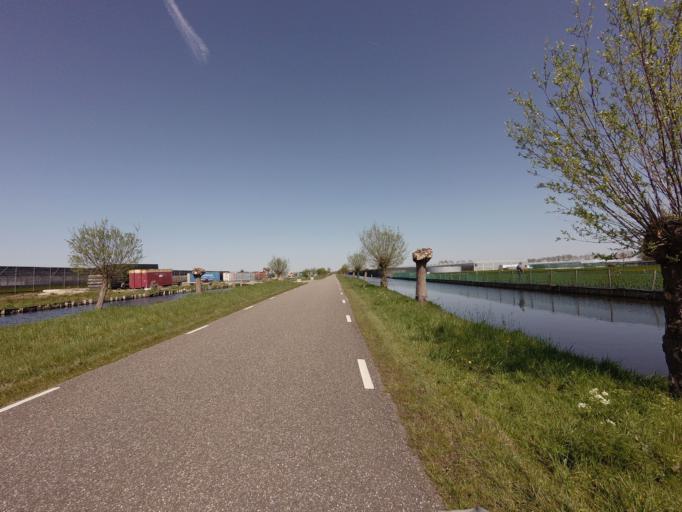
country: NL
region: South Holland
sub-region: Gemeente Boskoop
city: Boskoop
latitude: 52.0949
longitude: 4.6572
